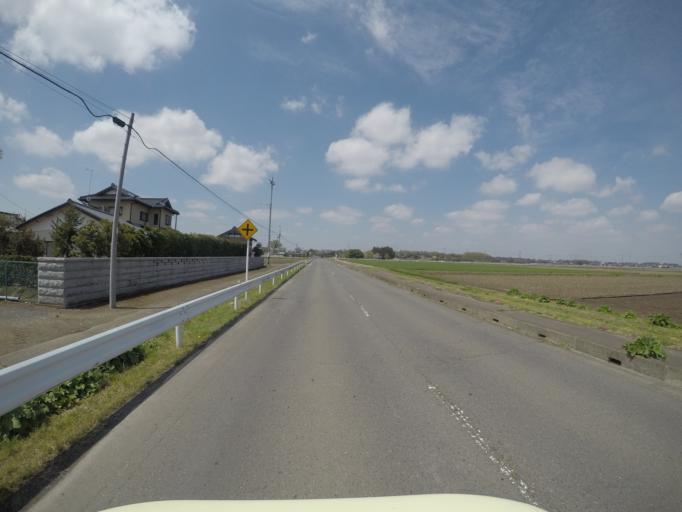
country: JP
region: Ibaraki
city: Shimodate
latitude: 36.3374
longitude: 139.9867
